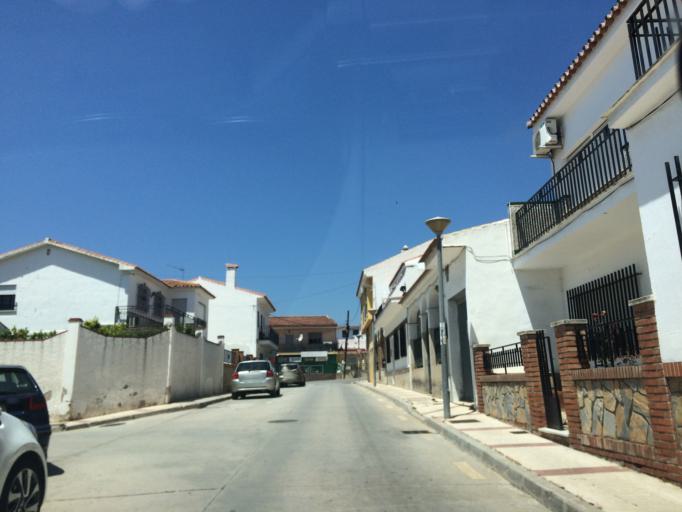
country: ES
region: Andalusia
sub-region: Provincia de Malaga
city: Malaga
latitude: 36.7351
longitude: -4.4804
